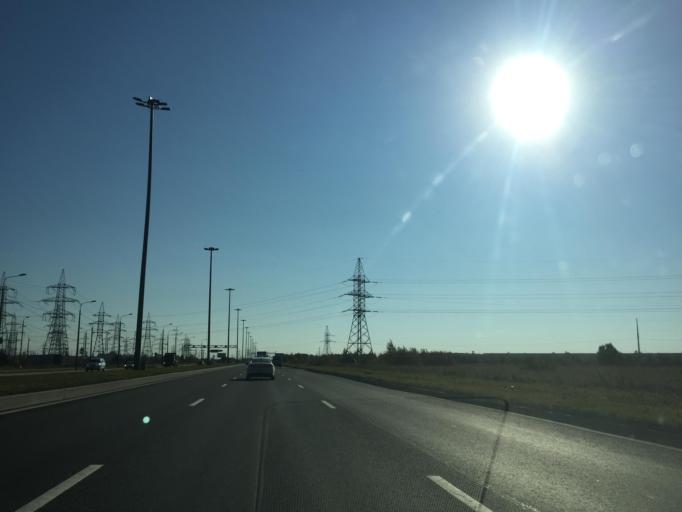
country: RU
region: St.-Petersburg
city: Petro-Slavyanka
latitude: 59.7551
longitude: 30.5204
